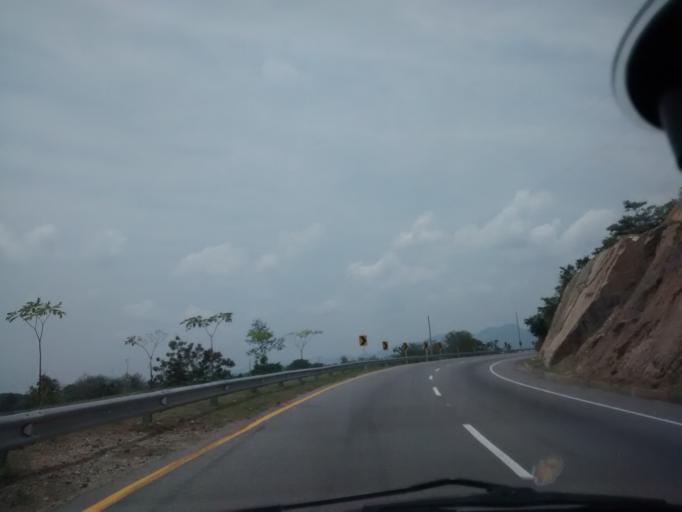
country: CO
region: Tolima
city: Espinal
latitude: 4.2208
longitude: -74.9730
